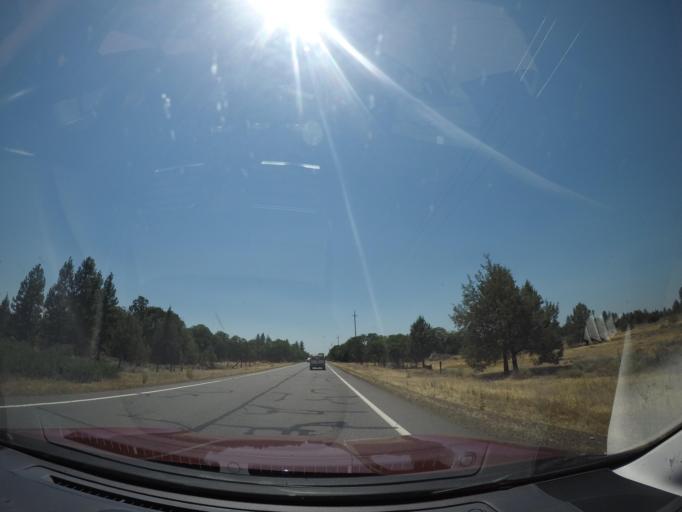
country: US
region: California
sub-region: Shasta County
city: Burney
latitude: 41.0939
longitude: -121.3045
